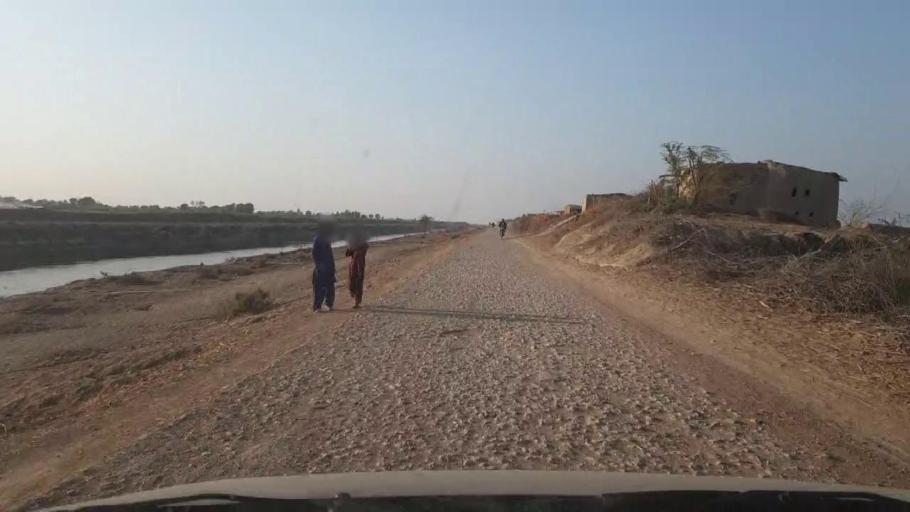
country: PK
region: Sindh
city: Samaro
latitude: 25.2817
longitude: 69.3400
